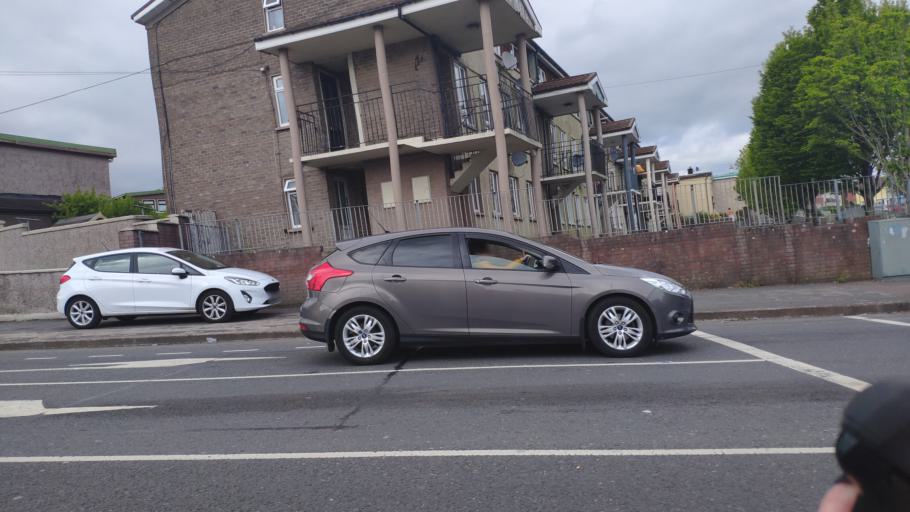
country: IE
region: Munster
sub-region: County Cork
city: Cork
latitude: 51.9068
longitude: -8.4963
